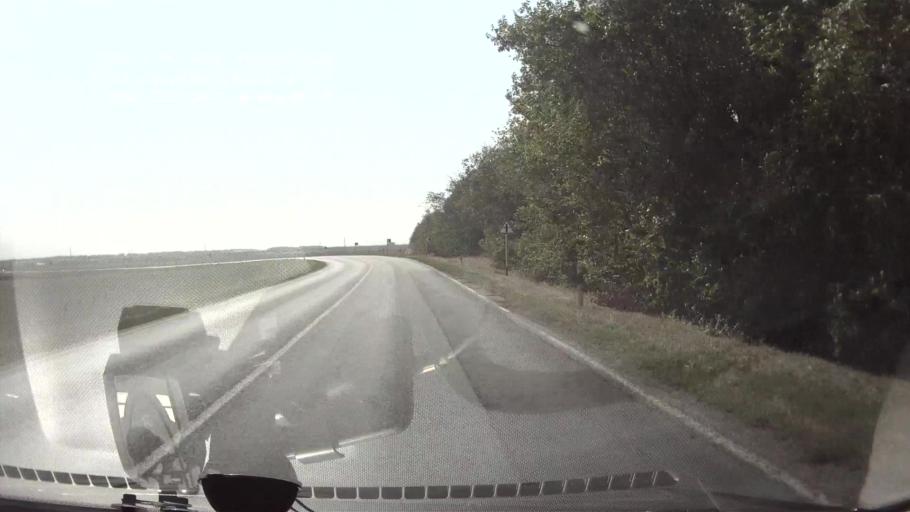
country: RU
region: Krasnodarskiy
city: Dmitriyevskaya
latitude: 45.6663
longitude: 40.7440
